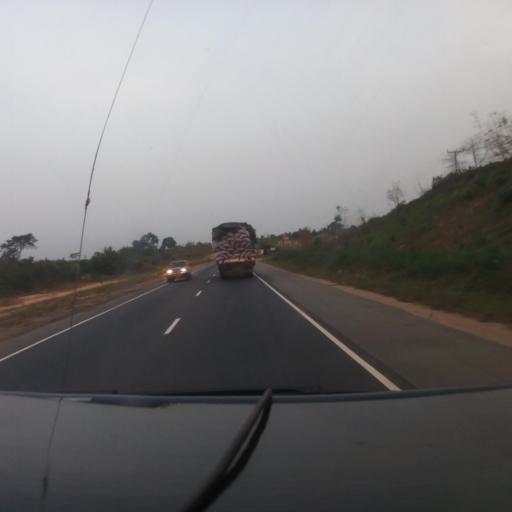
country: GH
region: Eastern
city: Nsawam
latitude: 5.8870
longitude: -0.3789
